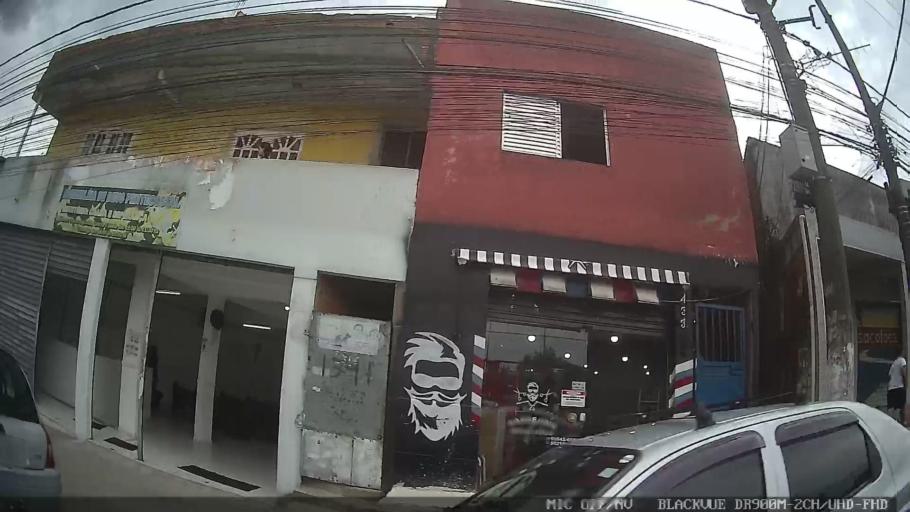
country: BR
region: Sao Paulo
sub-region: Itaquaquecetuba
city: Itaquaquecetuba
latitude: -23.4629
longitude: -46.3213
